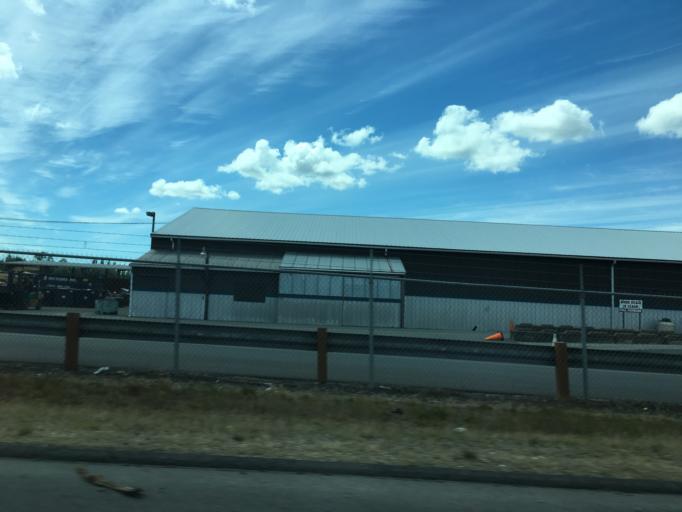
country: US
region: Washington
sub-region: Whatcom County
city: Lynden
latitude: 48.8646
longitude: -122.4860
